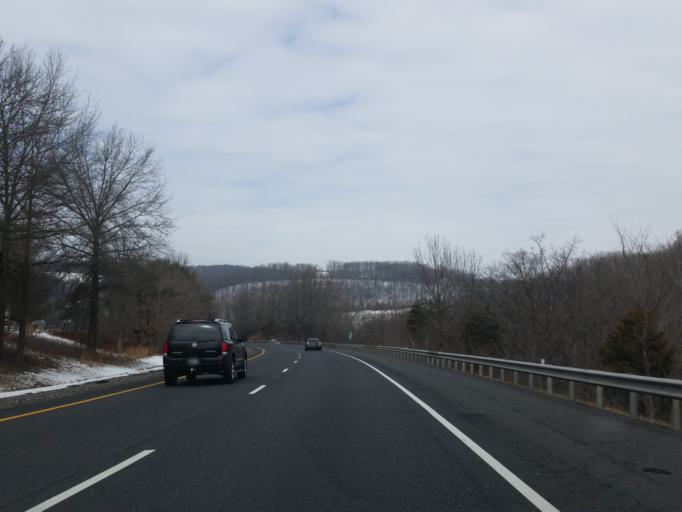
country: US
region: Maryland
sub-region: Baltimore County
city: Hunt Valley
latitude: 39.6096
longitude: -76.6579
